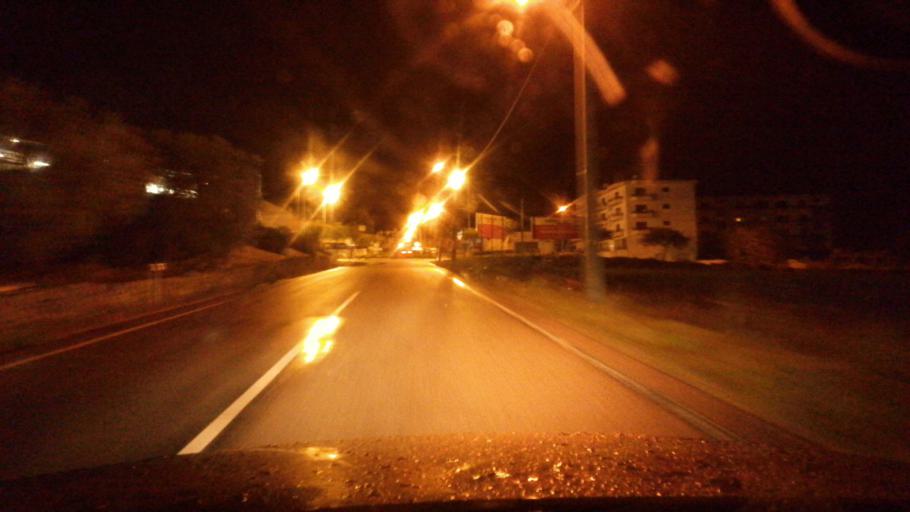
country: PT
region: Viseu
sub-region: Moimenta da Beira
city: Moimenta da Beira
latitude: 40.9693
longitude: -7.6065
